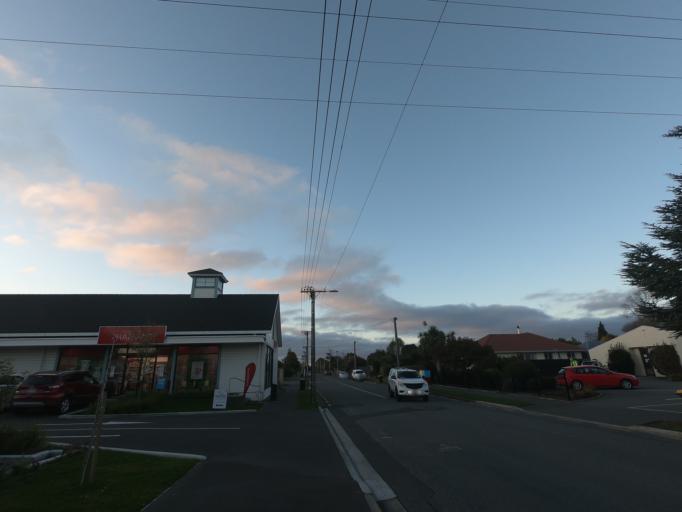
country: NZ
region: Canterbury
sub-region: Selwyn District
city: Prebbleton
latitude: -43.5746
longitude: 172.5678
